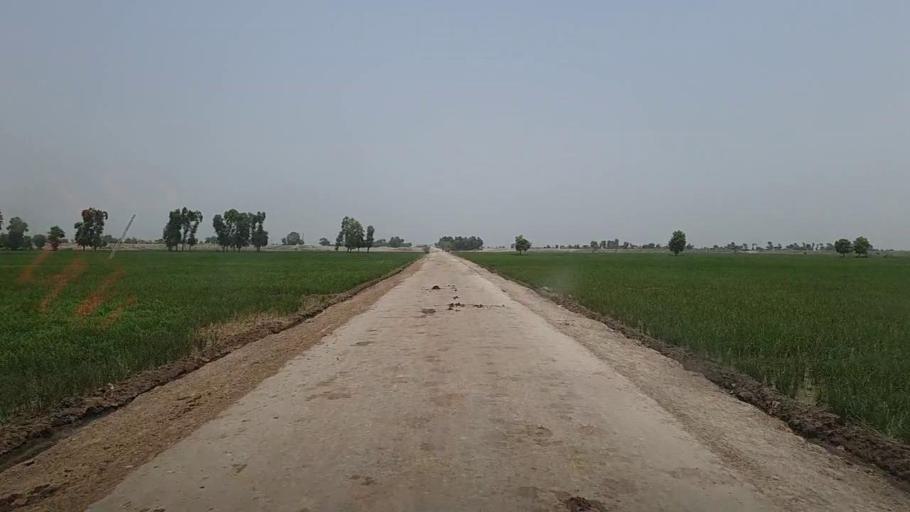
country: PK
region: Sindh
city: Sita Road
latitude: 27.0456
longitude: 67.8468
